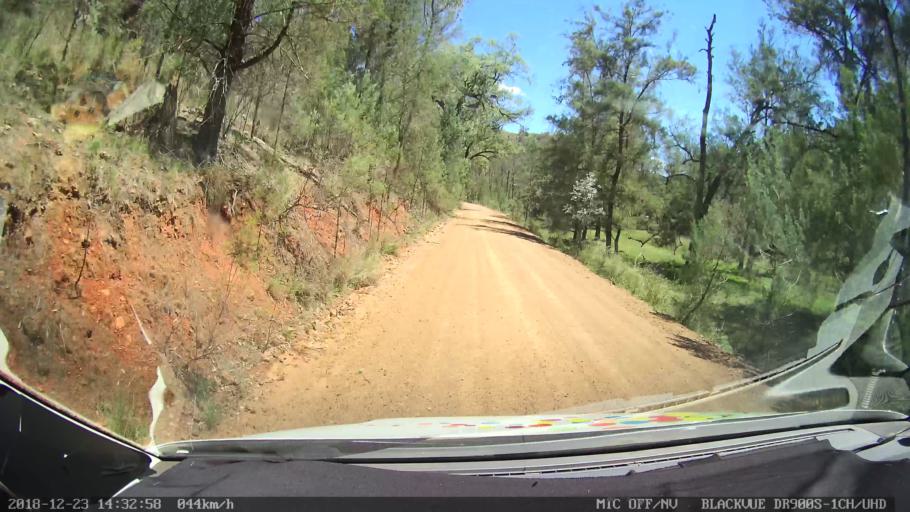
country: AU
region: New South Wales
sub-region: Tamworth Municipality
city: Manilla
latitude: -30.6052
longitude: 150.9153
